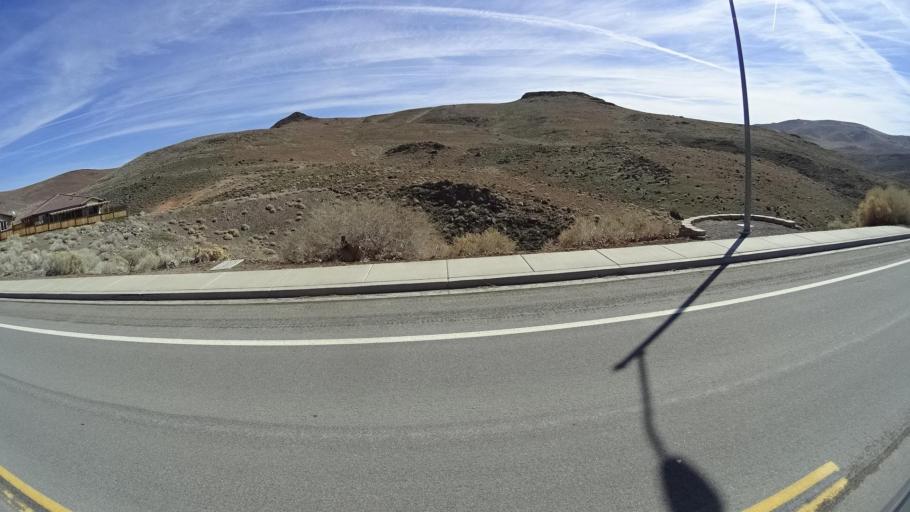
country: US
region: Nevada
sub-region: Washoe County
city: Spanish Springs
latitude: 39.5799
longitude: -119.6880
